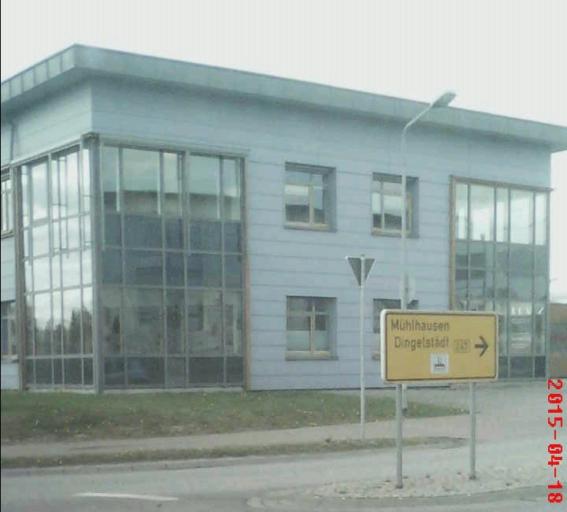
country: DE
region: Thuringia
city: Leinefelde
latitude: 51.3878
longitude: 10.3416
